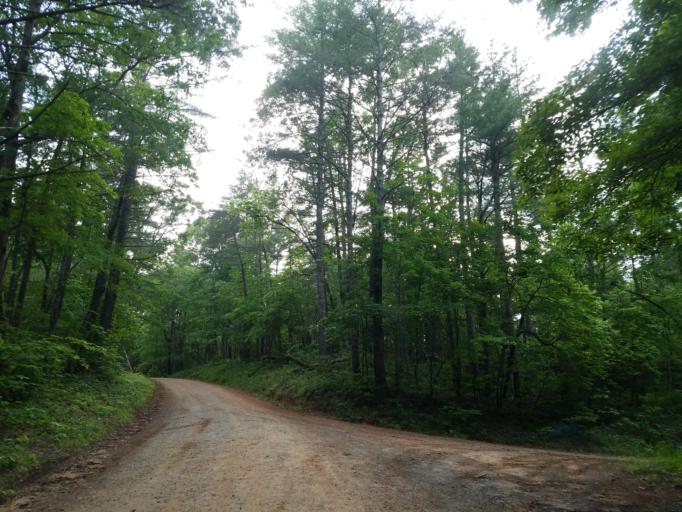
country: US
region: Georgia
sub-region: Lumpkin County
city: Dahlonega
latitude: 34.6044
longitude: -84.1054
